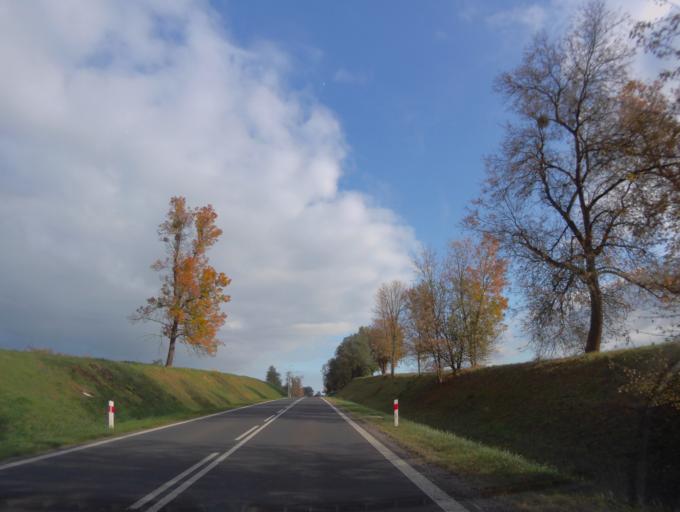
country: PL
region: Lublin Voivodeship
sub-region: Powiat bilgorajski
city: Goraj
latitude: 50.7765
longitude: 22.6765
